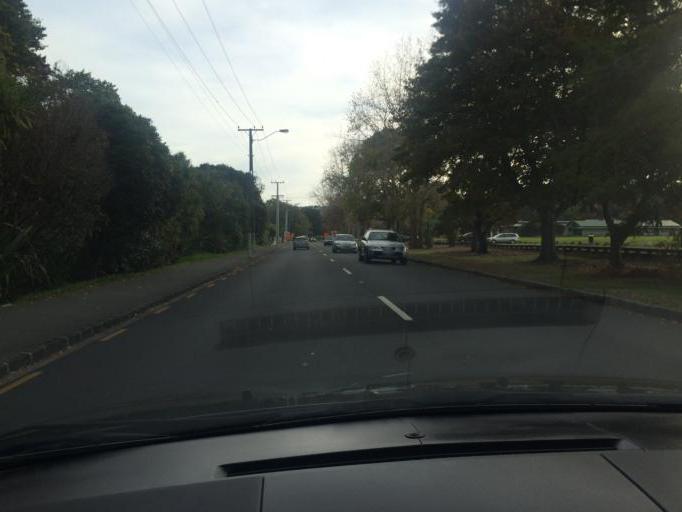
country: NZ
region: Auckland
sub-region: Auckland
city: Auckland
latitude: -36.8651
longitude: 174.7935
